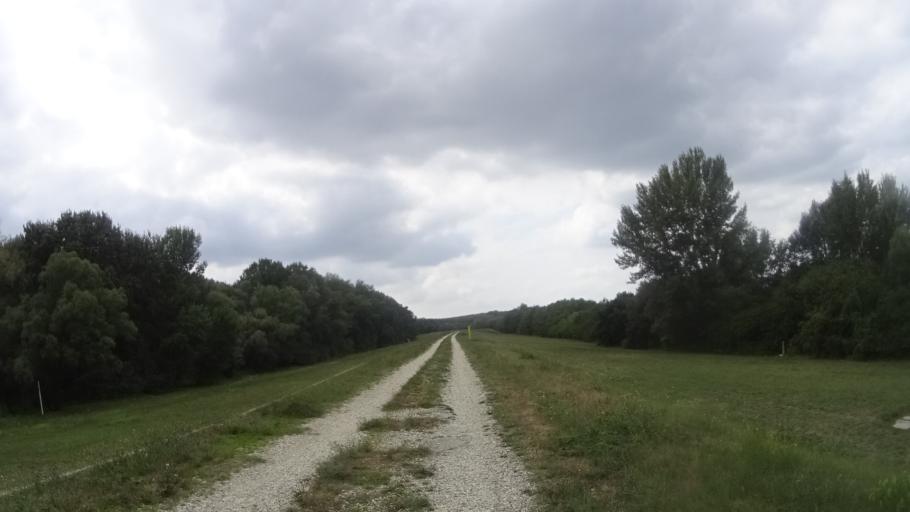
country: SK
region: Trnavsky
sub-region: Okres Dunajska Streda
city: Velky Meder
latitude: 47.7545
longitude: 17.7852
